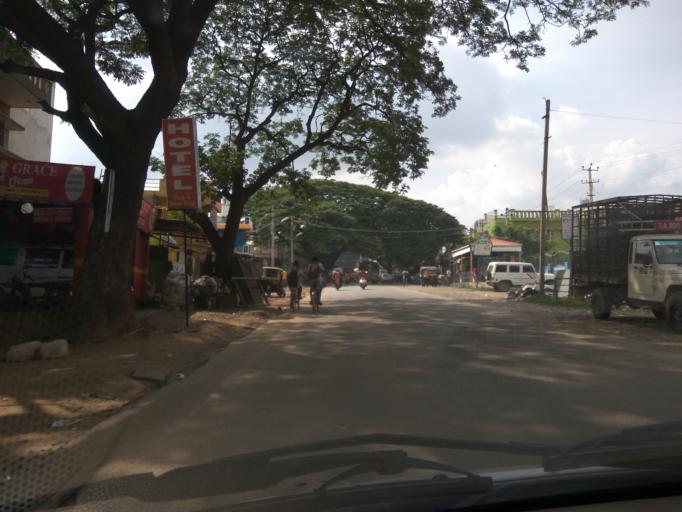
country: IN
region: Karnataka
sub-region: Kolar
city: Kolar
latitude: 13.1312
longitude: 78.1278
